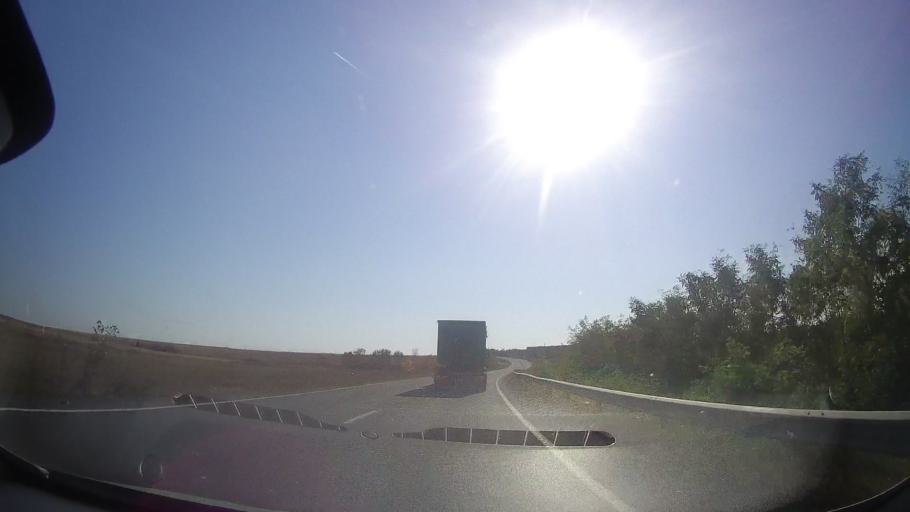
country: RO
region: Timis
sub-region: Comuna Belint
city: Belint
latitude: 45.7738
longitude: 21.7017
